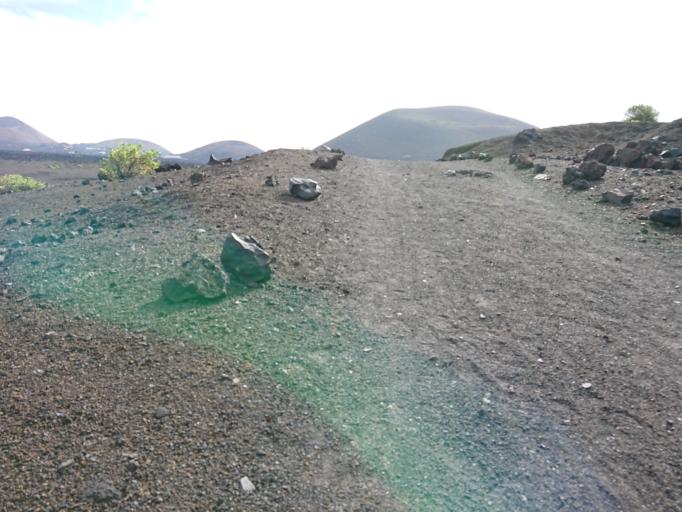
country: ES
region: Canary Islands
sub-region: Provincia de Las Palmas
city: Tias
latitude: 29.0054
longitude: -13.6759
